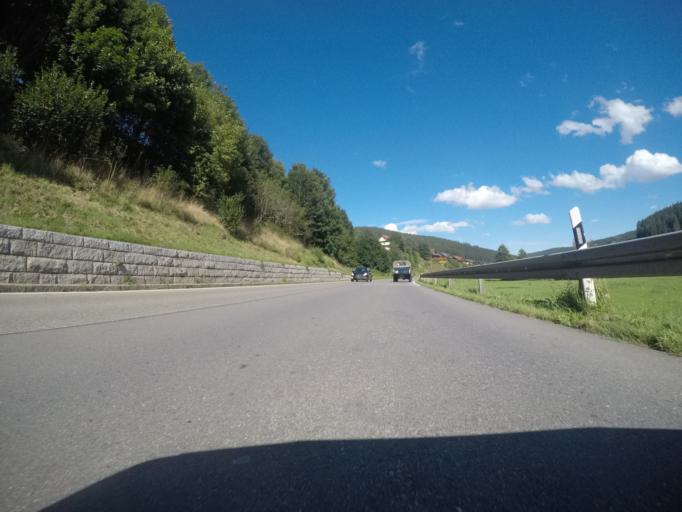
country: DE
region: Baden-Wuerttemberg
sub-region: Freiburg Region
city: Furtwangen im Schwarzwald
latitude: 48.0488
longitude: 8.2460
